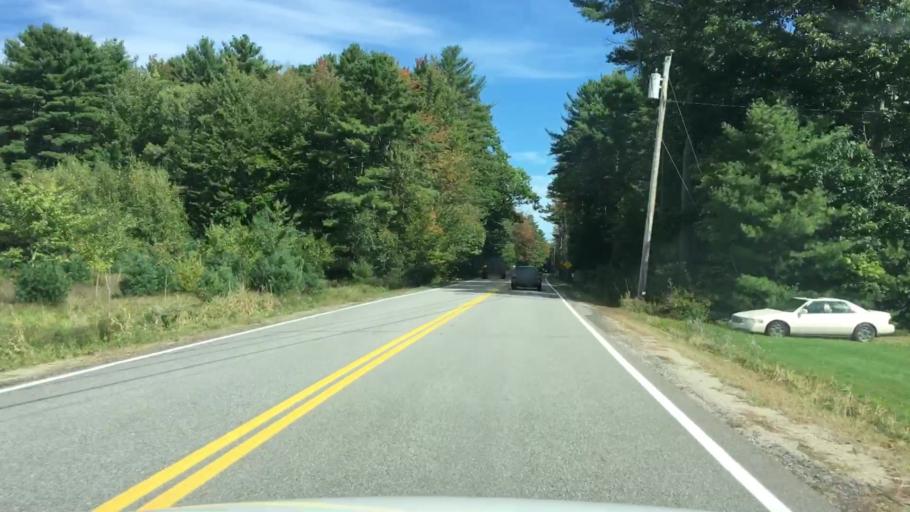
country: US
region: Maine
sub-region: Cumberland County
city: West Scarborough
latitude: 43.5870
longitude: -70.4441
